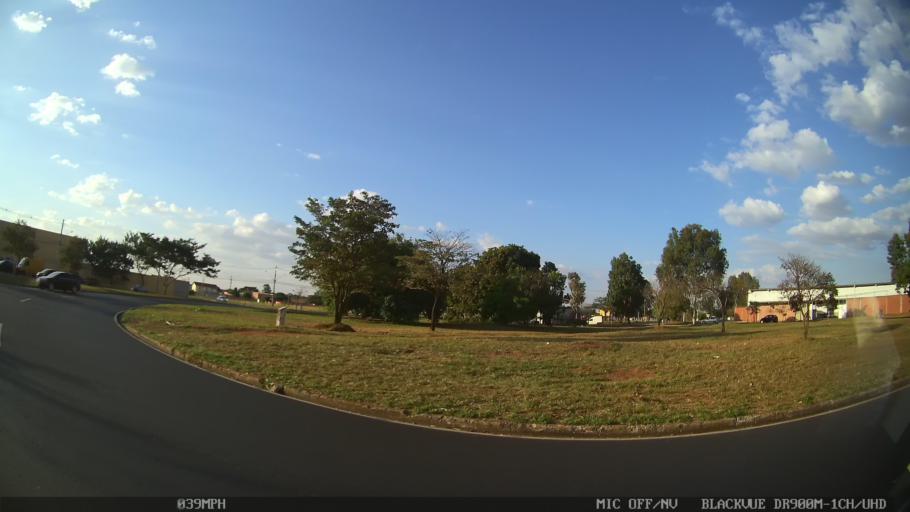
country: BR
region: Sao Paulo
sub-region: Ribeirao Preto
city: Ribeirao Preto
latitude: -21.1632
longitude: -47.7420
